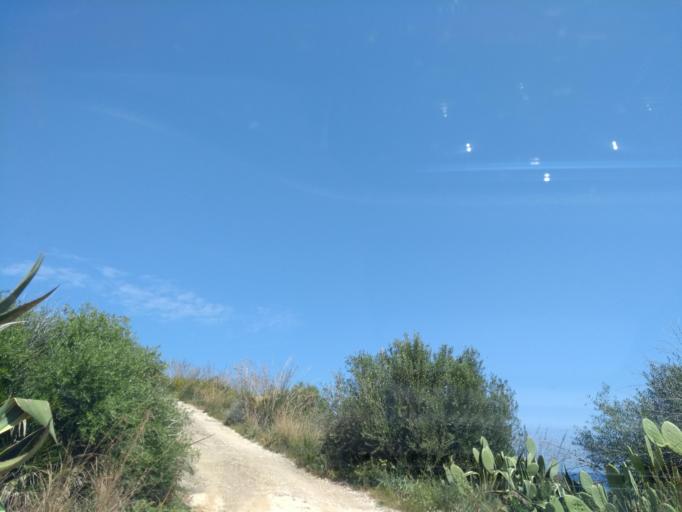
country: IT
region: Sicily
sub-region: Trapani
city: Castellammare del Golfo
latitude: 38.0513
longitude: 12.8504
